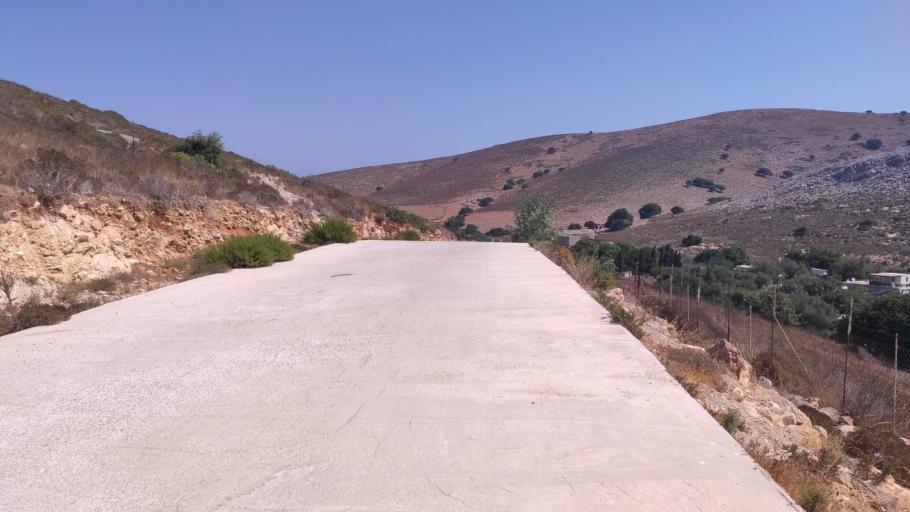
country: GR
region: South Aegean
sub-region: Nomos Dodekanisou
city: Pylion
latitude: 36.9355
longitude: 27.1343
